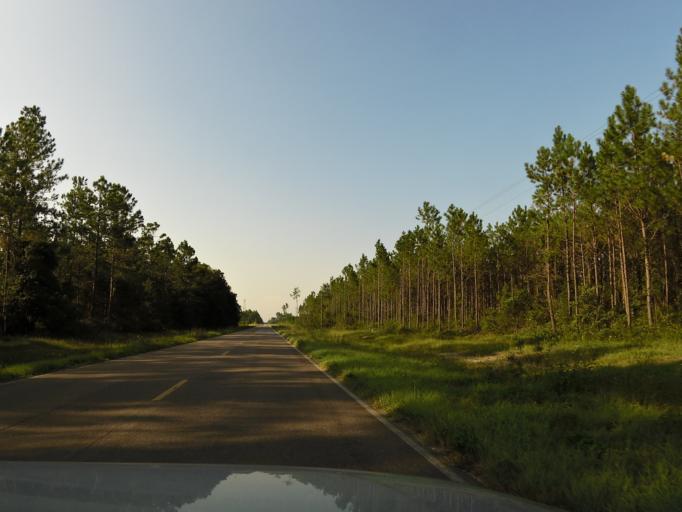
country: US
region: Florida
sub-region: Duval County
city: Baldwin
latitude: 30.3249
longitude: -82.0086
